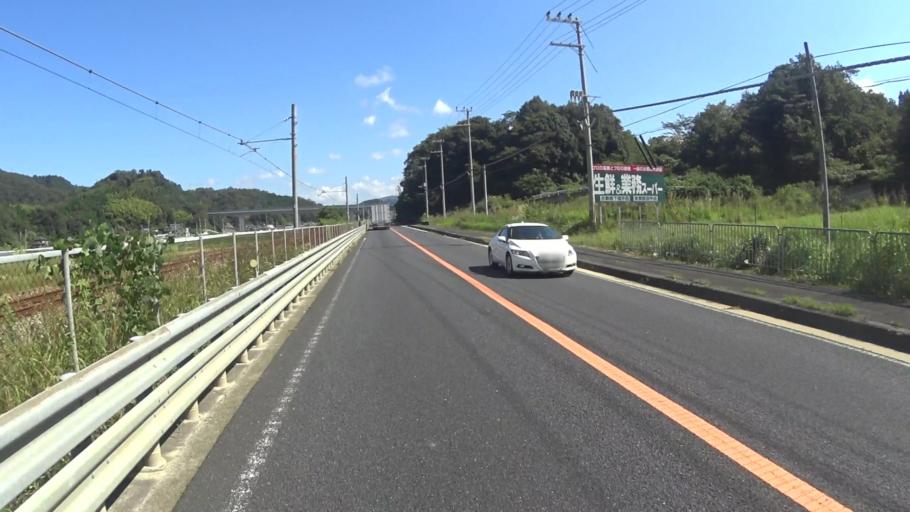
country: JP
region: Kyoto
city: Ayabe
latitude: 35.3339
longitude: 135.3025
